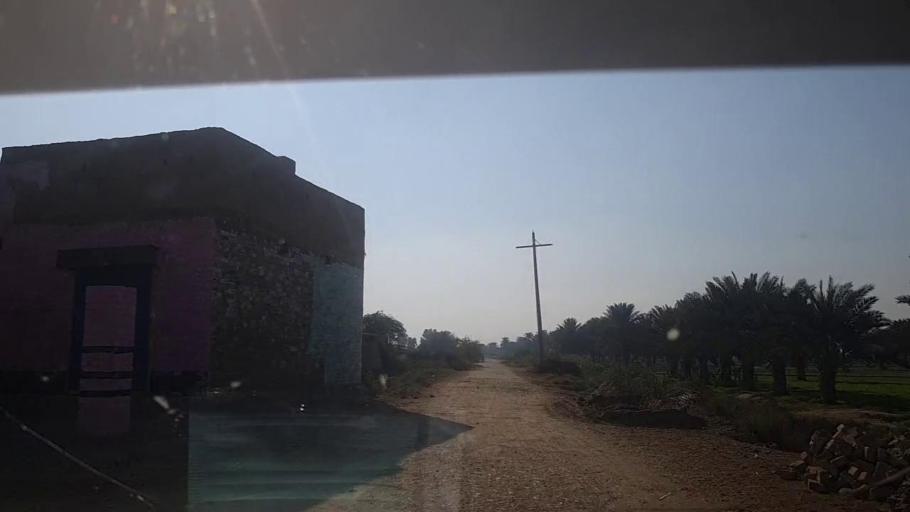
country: PK
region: Sindh
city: Gambat
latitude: 27.3680
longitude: 68.5625
